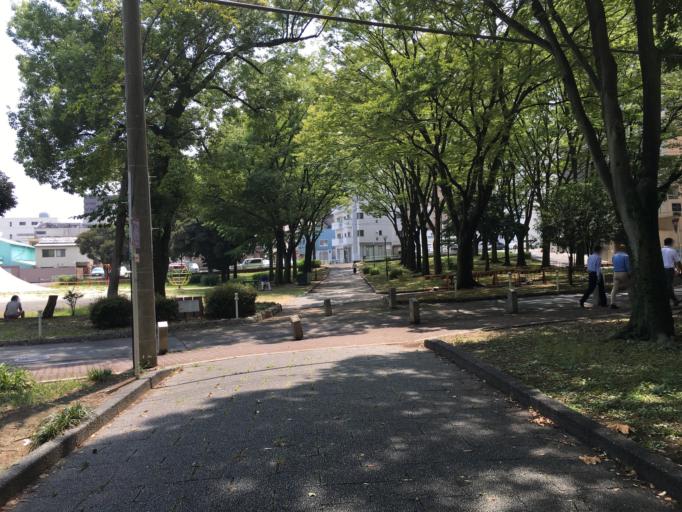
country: JP
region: Aichi
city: Nagoya-shi
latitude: 35.1481
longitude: 136.9042
